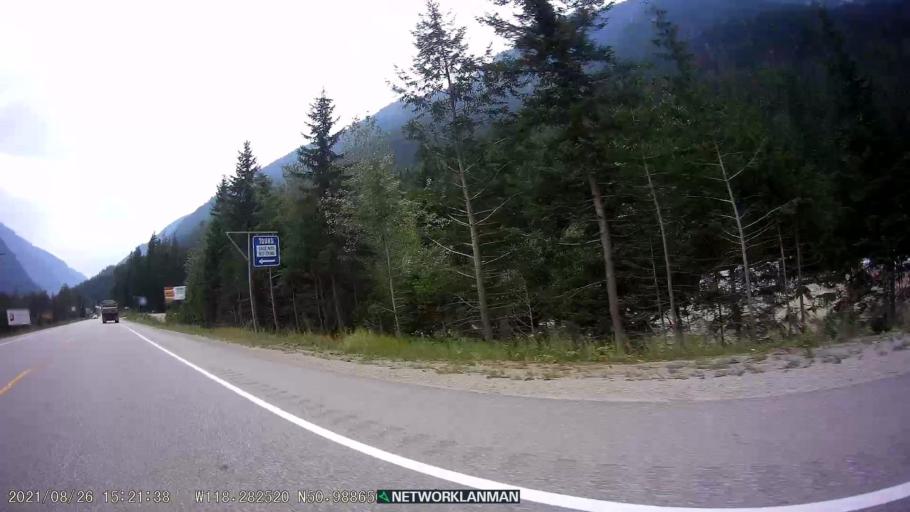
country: CA
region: British Columbia
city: Revelstoke
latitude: 50.9886
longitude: -118.2831
